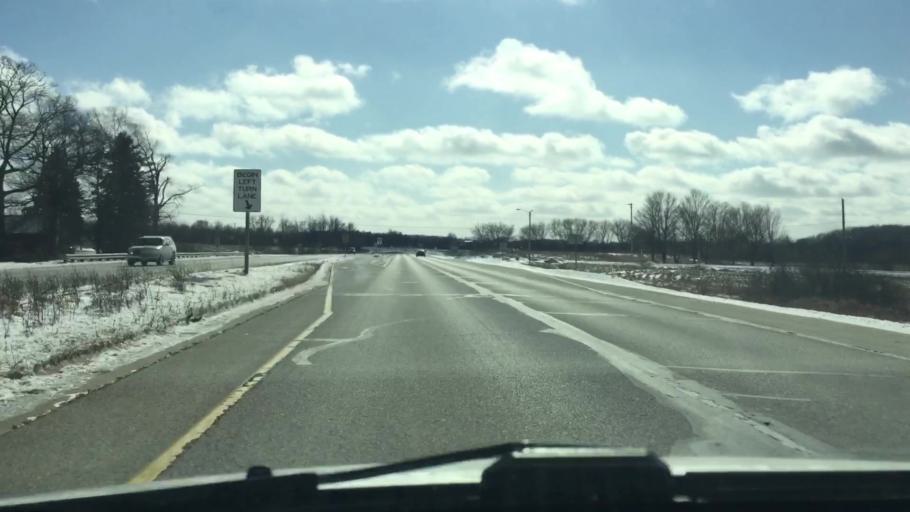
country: US
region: Wisconsin
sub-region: Waukesha County
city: Big Bend
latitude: 42.9315
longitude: -88.2287
